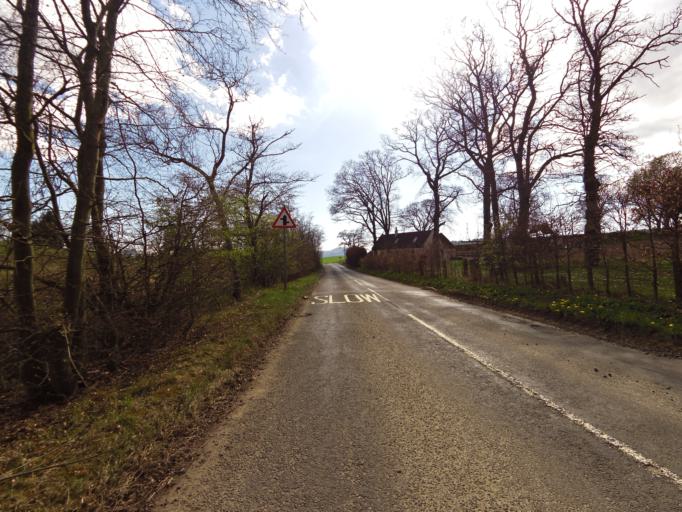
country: GB
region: Scotland
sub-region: Fife
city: Auchtermuchty
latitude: 56.3139
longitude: -3.2345
